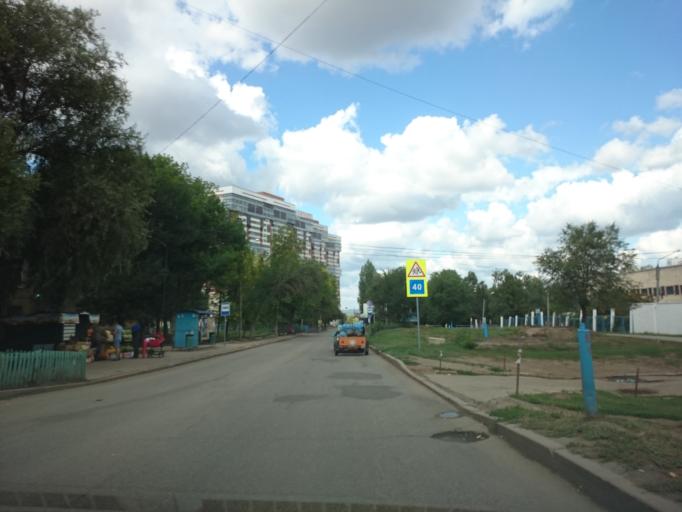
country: RU
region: Samara
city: Samara
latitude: 53.2348
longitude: 50.1854
